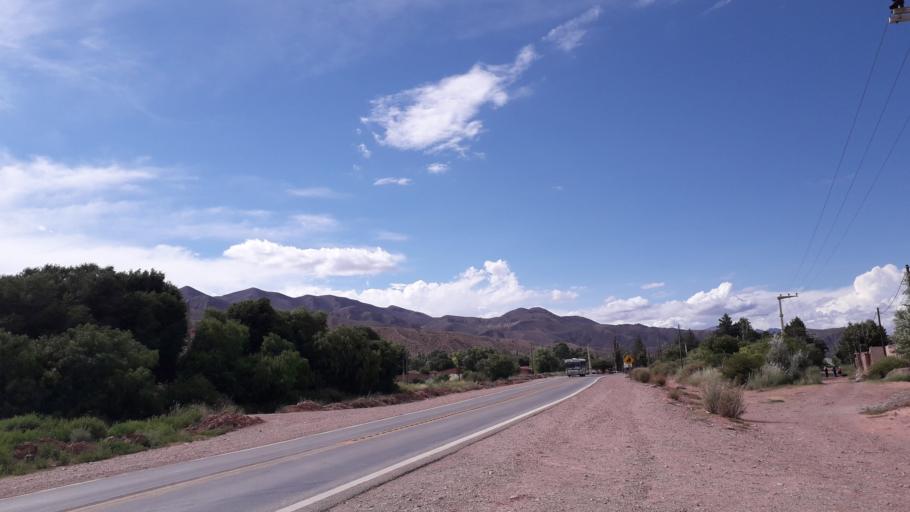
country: AR
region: Jujuy
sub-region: Departamento de Humahuaca
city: Humahuaca
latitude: -23.3078
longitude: -65.3535
